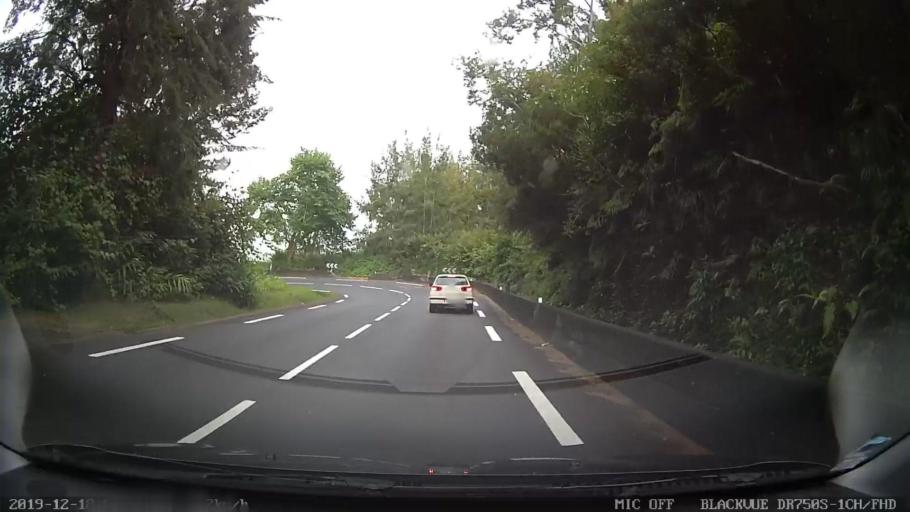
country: RE
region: Reunion
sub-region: Reunion
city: Cilaos
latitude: -21.1528
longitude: 55.6147
